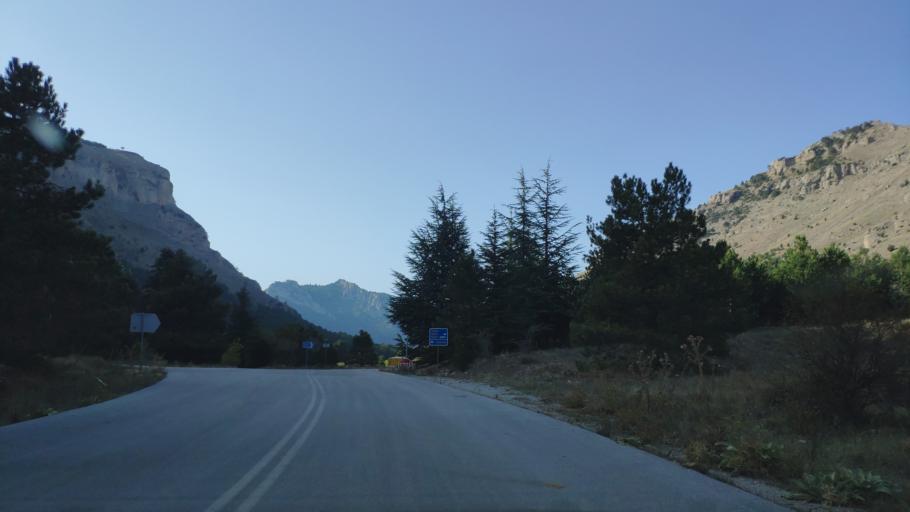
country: GR
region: West Greece
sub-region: Nomos Achaias
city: Aiyira
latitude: 38.0364
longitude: 22.3990
